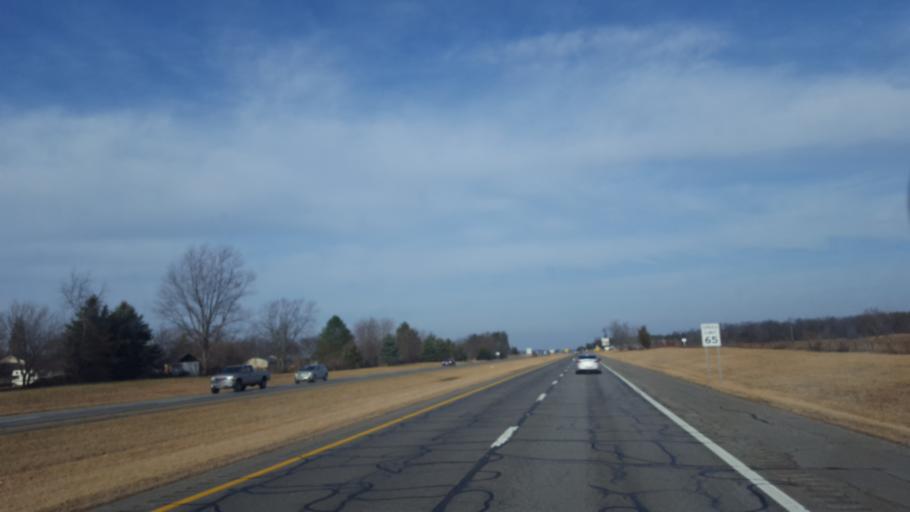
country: US
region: Ohio
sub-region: Marion County
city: Marion
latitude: 40.6987
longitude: -83.1573
